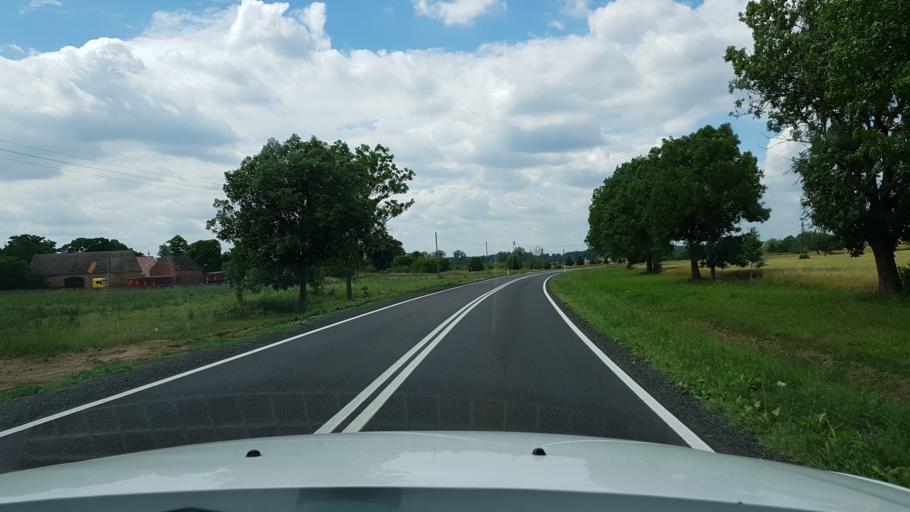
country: PL
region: West Pomeranian Voivodeship
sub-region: Powiat mysliborski
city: Boleszkowice
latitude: 52.7364
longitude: 14.5229
